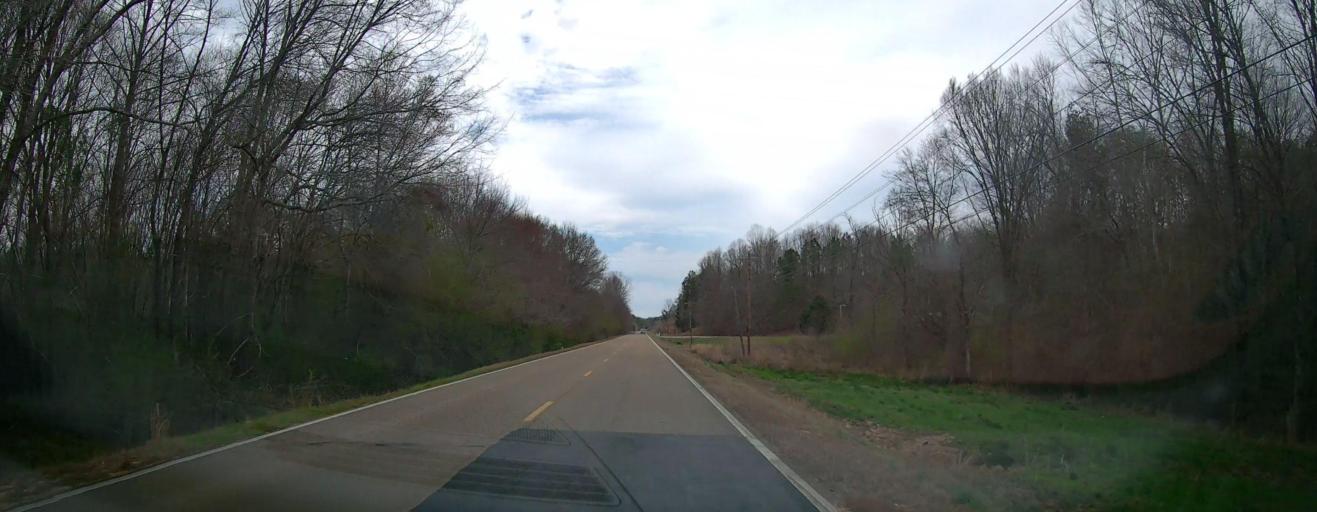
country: US
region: Mississippi
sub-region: Itawamba County
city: Fulton
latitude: 34.2575
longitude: -88.3163
